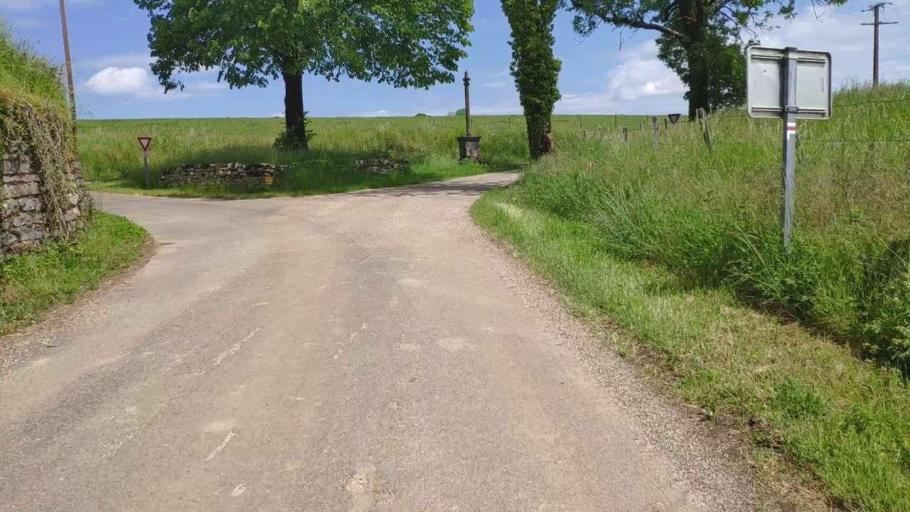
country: FR
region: Franche-Comte
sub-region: Departement du Jura
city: Perrigny
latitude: 46.7550
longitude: 5.6357
